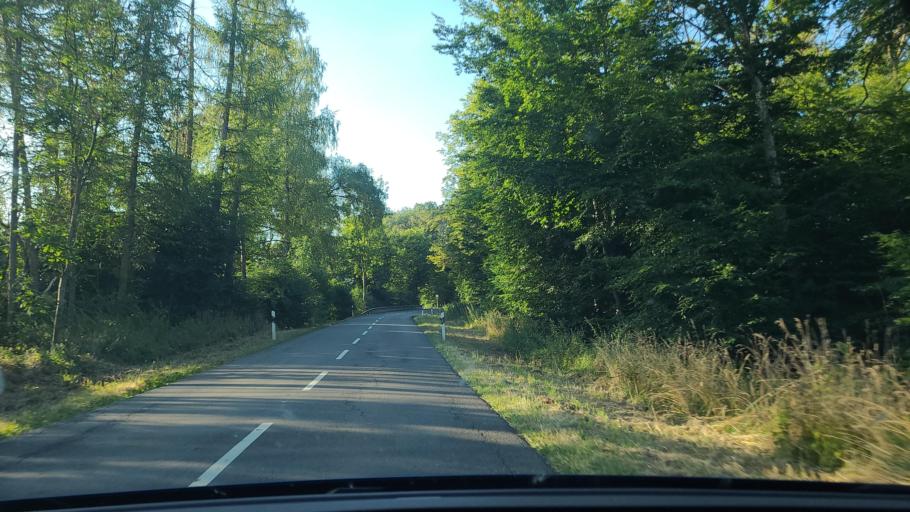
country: LU
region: Luxembourg
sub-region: Canton de Capellen
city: Dippach
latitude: 49.6101
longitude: 5.9915
